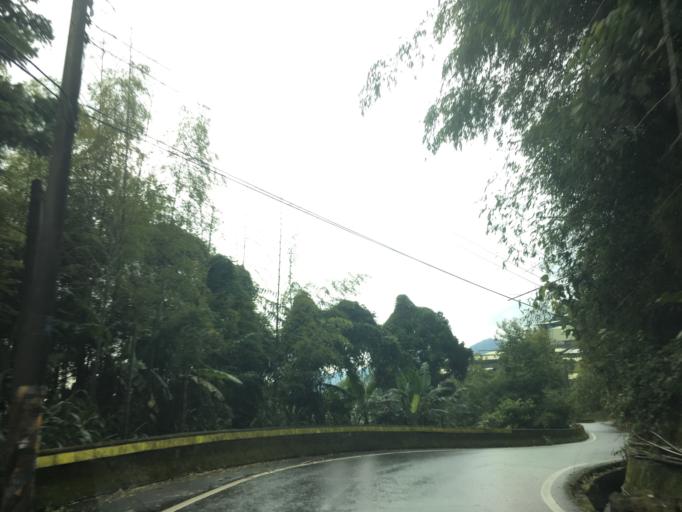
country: TW
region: Taiwan
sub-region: Chiayi
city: Jiayi Shi
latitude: 23.4460
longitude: 120.6680
